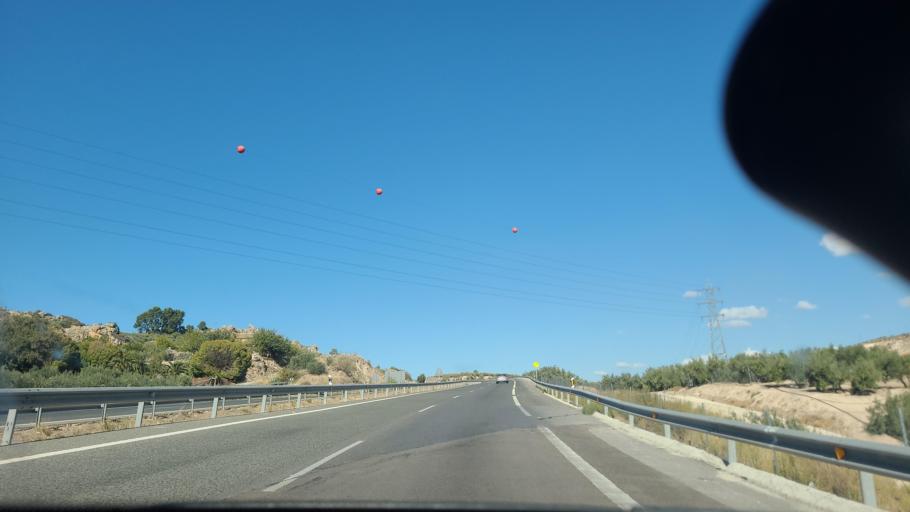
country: ES
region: Andalusia
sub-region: Provincia de Jaen
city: La Guardia de Jaen
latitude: 37.7374
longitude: -3.6850
